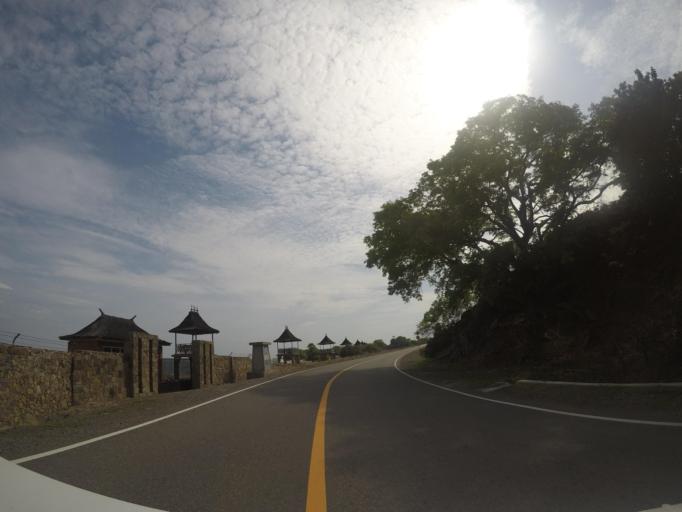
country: ID
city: Metinaro
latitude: -8.4788
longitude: 125.8461
